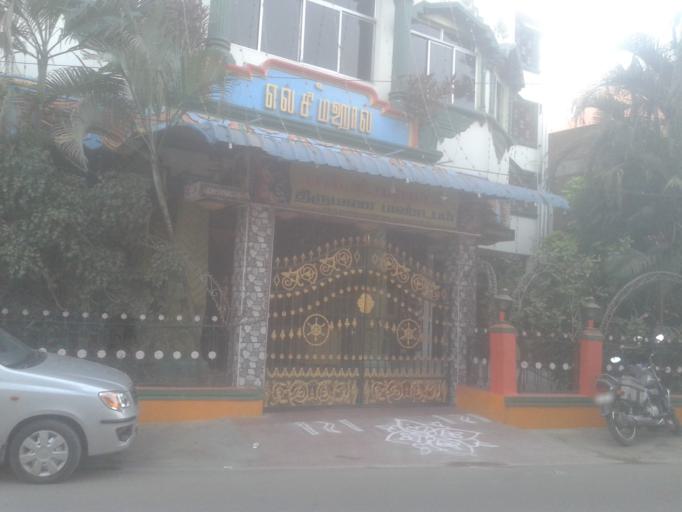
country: IN
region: Tamil Nadu
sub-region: Kancheepuram
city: Pallavaram
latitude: 12.9746
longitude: 80.1324
